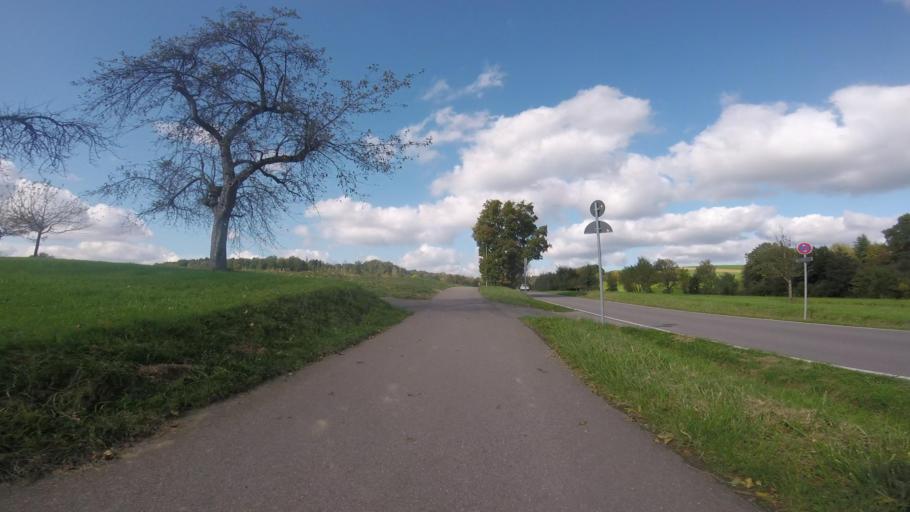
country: DE
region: Baden-Wuerttemberg
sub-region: Regierungsbezirk Stuttgart
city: Aspach
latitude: 48.9740
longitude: 9.3992
